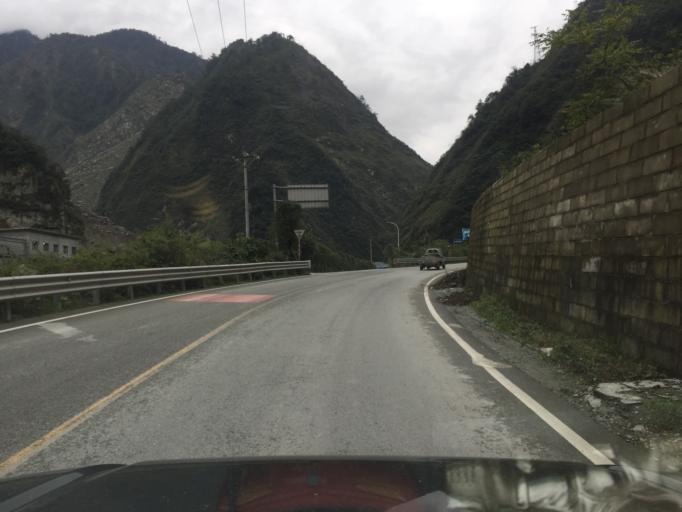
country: CN
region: Sichuan
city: Guangsheng
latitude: 31.0611
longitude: 103.4084
